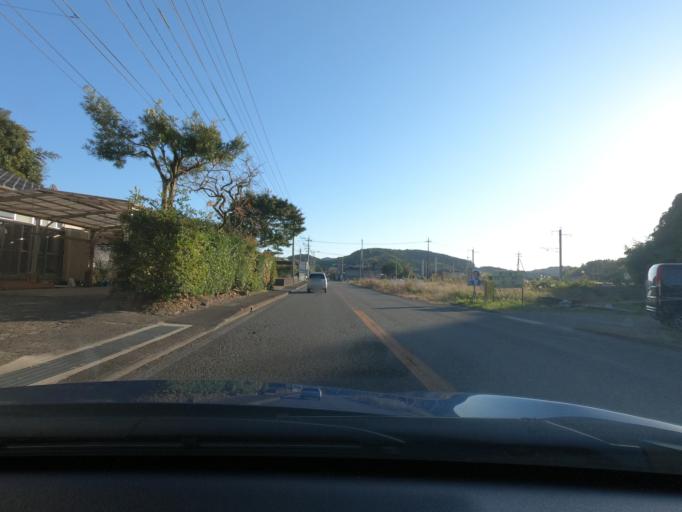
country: JP
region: Kagoshima
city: Satsumasendai
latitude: 31.8682
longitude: 130.2249
